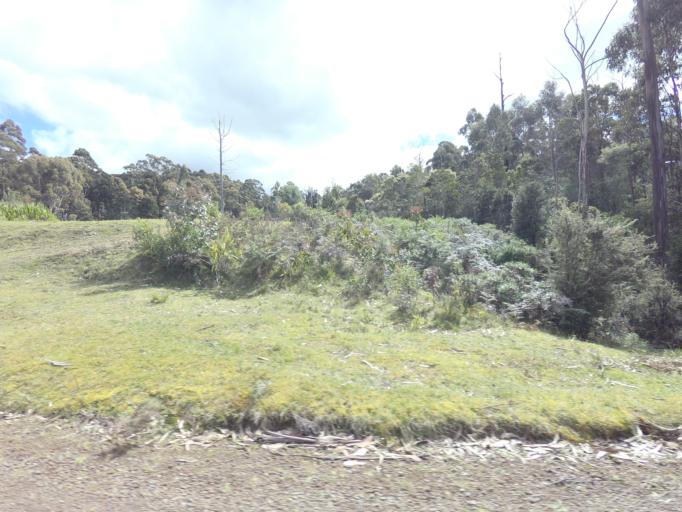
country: AU
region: Tasmania
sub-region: Huon Valley
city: Geeveston
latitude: -43.4211
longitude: 147.0124
